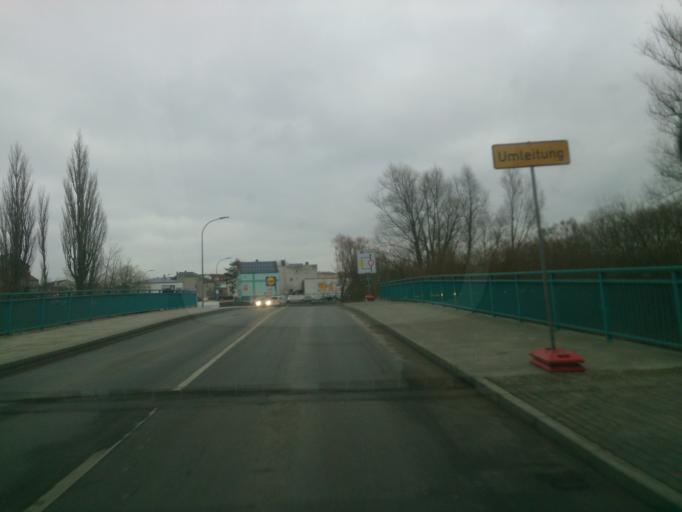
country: DE
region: Mecklenburg-Vorpommern
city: Demmin
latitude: 53.8992
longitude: 13.0419
